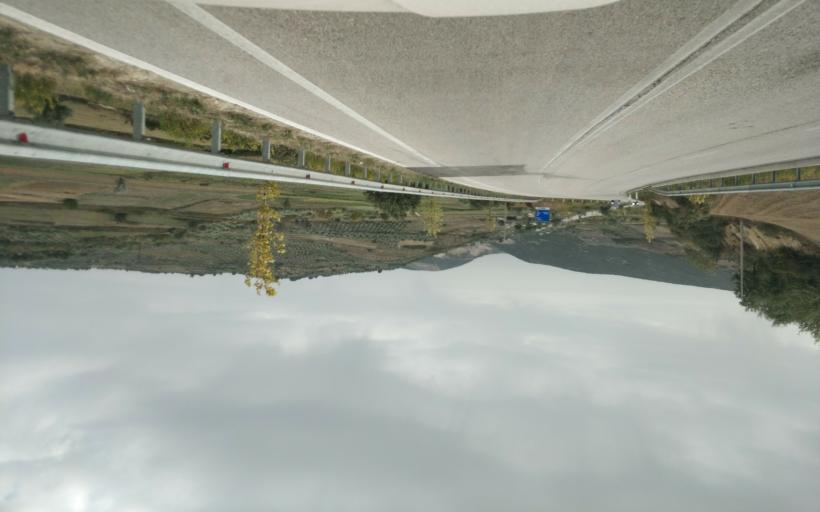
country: AL
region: Fier
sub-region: Rrethi i Mallakastres
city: Fratar
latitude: 40.4950
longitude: 19.8287
